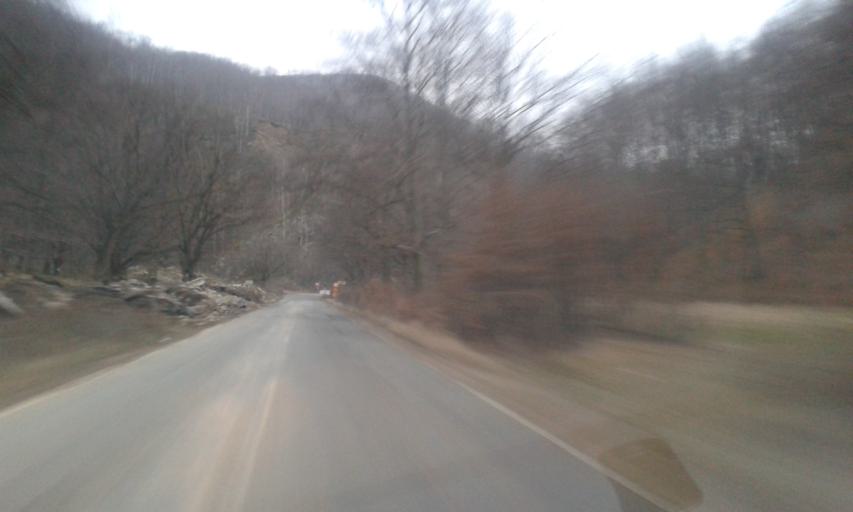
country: RO
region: Gorj
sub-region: Comuna Bumbesti-Jiu
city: Bumbesti-Jiu
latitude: 45.2583
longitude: 23.3887
